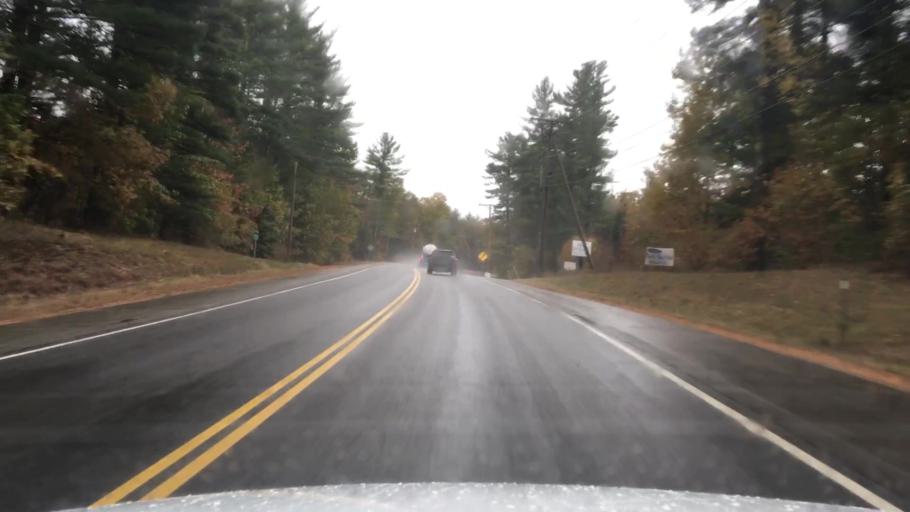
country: US
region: New Hampshire
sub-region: Strafford County
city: Barrington
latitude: 43.2307
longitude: -70.9922
